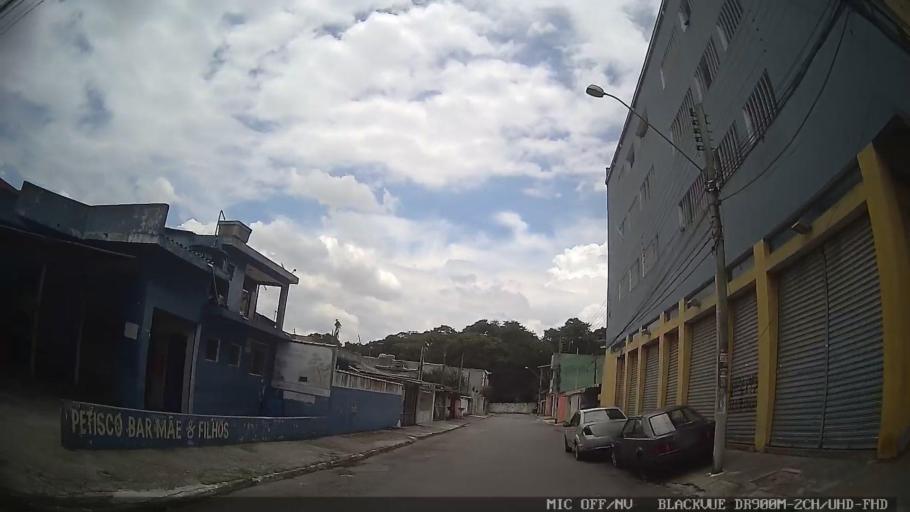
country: BR
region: Sao Paulo
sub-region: Aruja
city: Aruja
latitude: -23.4198
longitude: -46.3678
